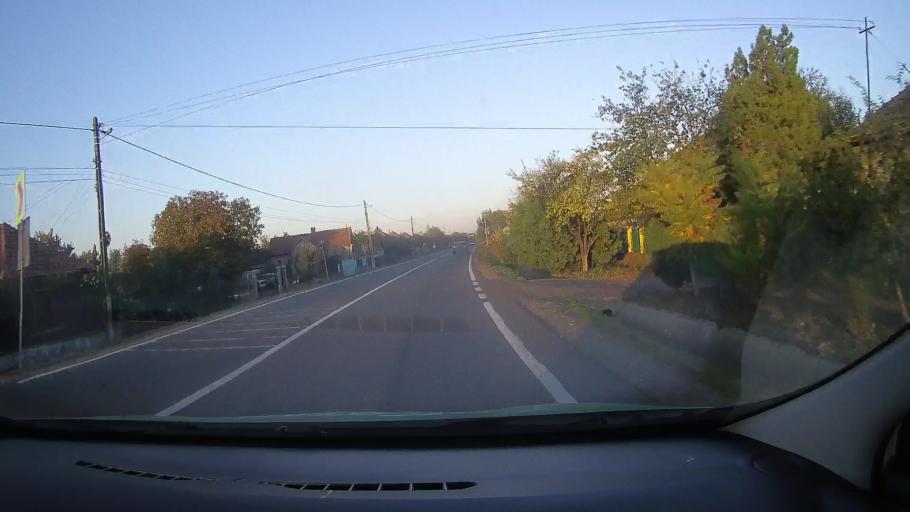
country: RO
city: Dioszeg
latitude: 47.2823
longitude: 21.9867
